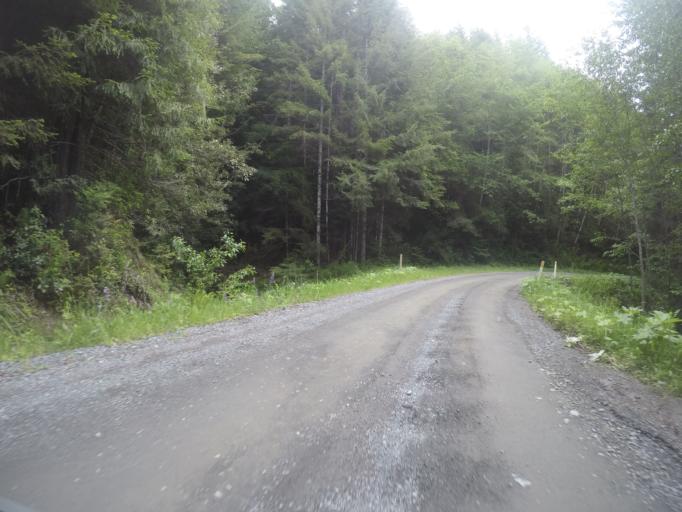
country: US
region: California
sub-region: Humboldt County
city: Westhaven-Moonstone
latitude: 41.2344
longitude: -123.9900
